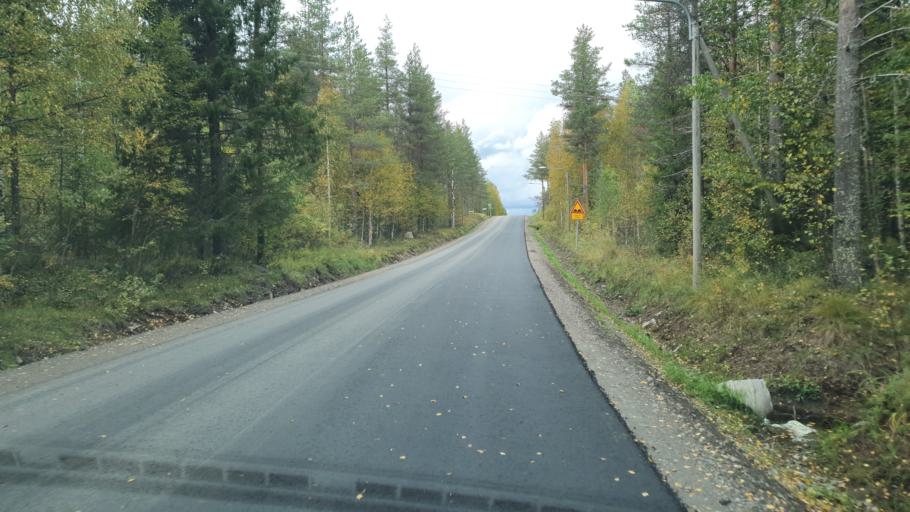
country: FI
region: Lapland
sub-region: Rovaniemi
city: Rovaniemi
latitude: 66.4252
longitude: 25.3987
